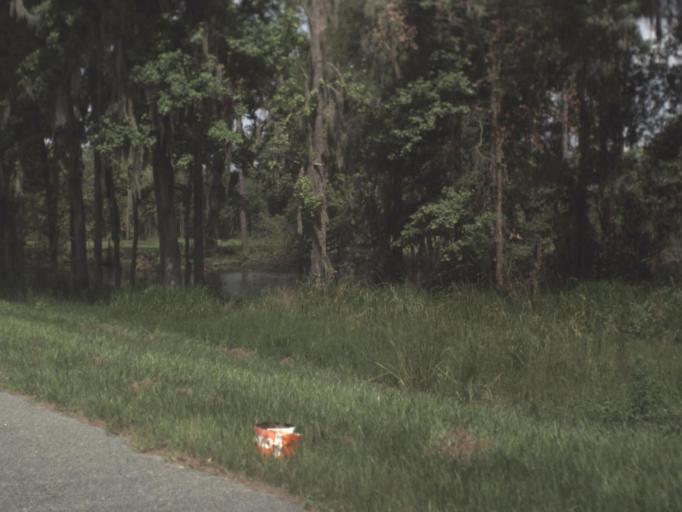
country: US
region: Florida
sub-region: Madison County
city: Madison
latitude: 30.4865
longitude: -83.5214
